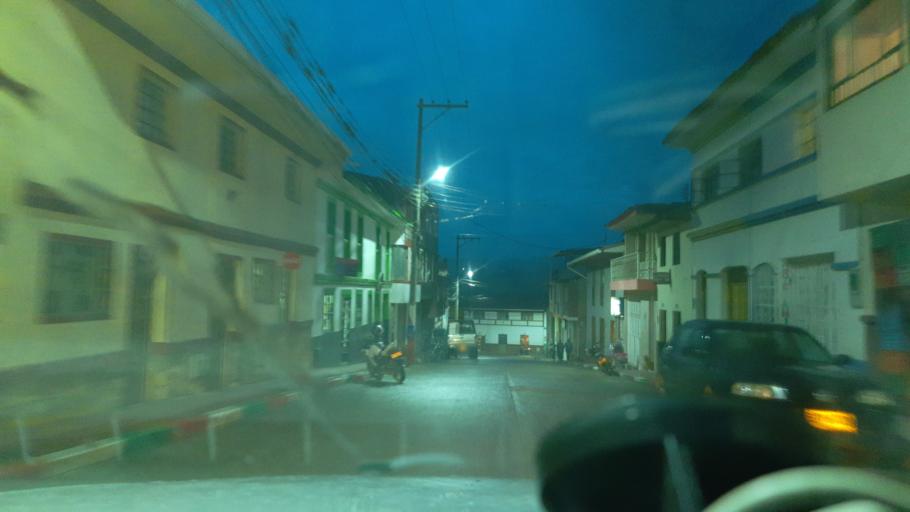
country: CO
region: Boyaca
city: Tibana
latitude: 5.3185
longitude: -73.3964
